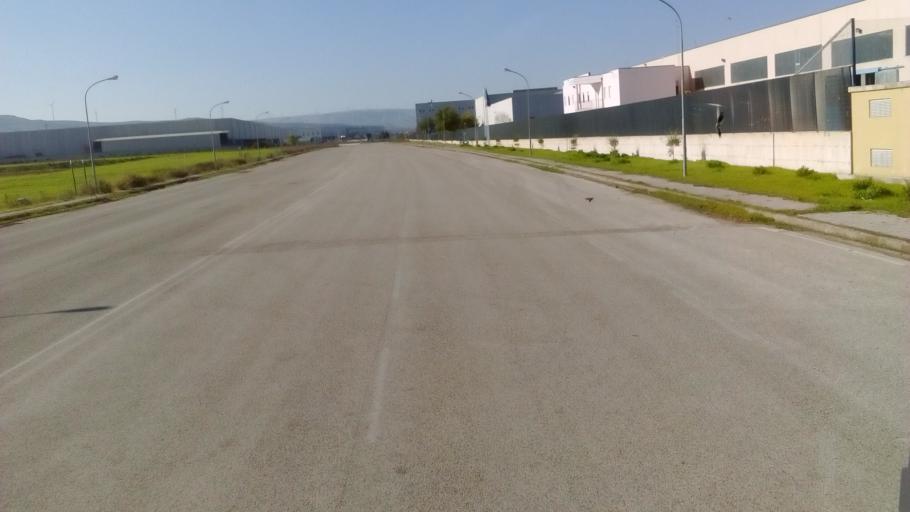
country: IT
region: Basilicate
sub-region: Provincia di Potenza
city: Melfi
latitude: 41.0782
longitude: 15.6640
